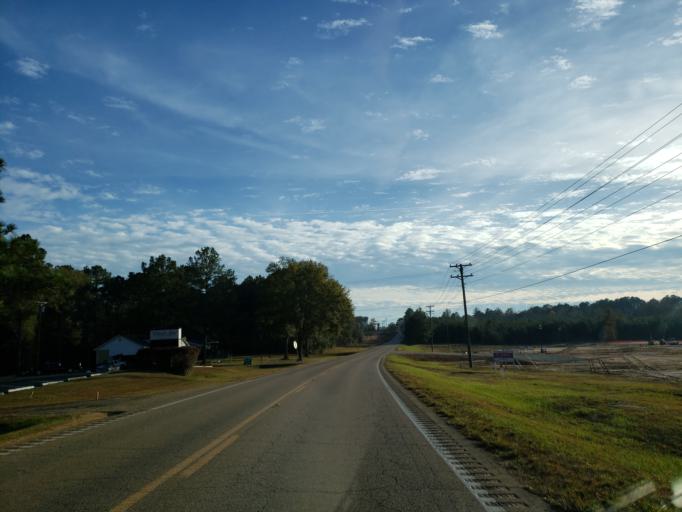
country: US
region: Mississippi
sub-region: Lamar County
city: West Hattiesburg
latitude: 31.2976
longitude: -89.4692
